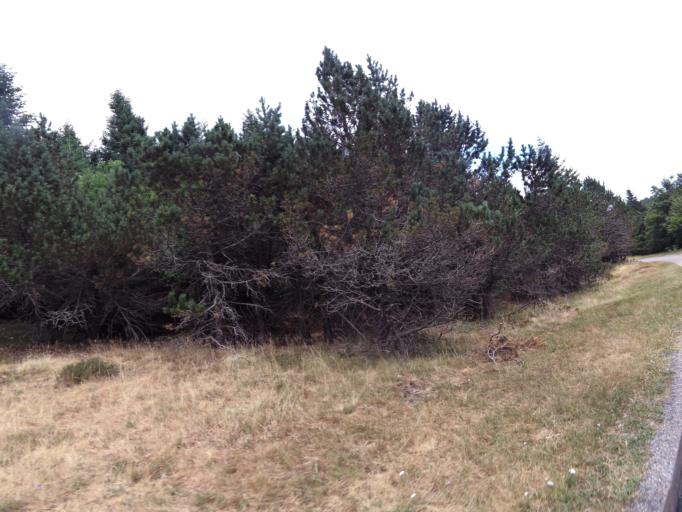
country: FR
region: Languedoc-Roussillon
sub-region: Departement du Gard
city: Valleraugue
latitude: 44.0678
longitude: 3.5924
